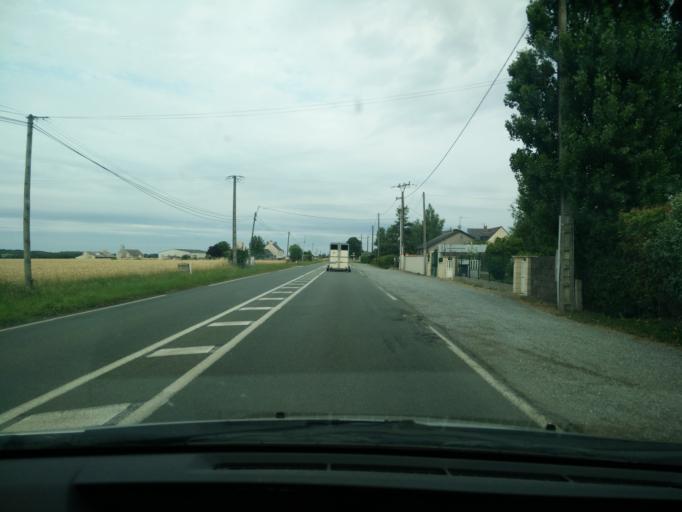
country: FR
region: Pays de la Loire
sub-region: Departement de Maine-et-Loire
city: Brissac-Quince
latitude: 47.3217
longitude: -0.4117
